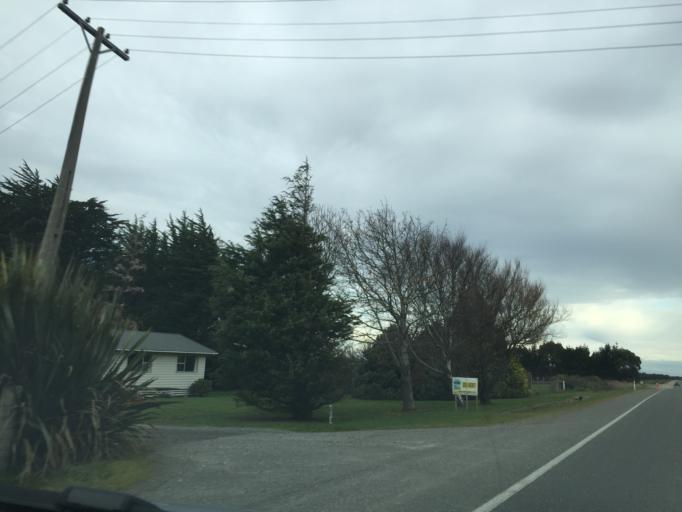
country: NZ
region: Southland
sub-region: Invercargill City
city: Invercargill
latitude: -46.3588
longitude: 168.5441
